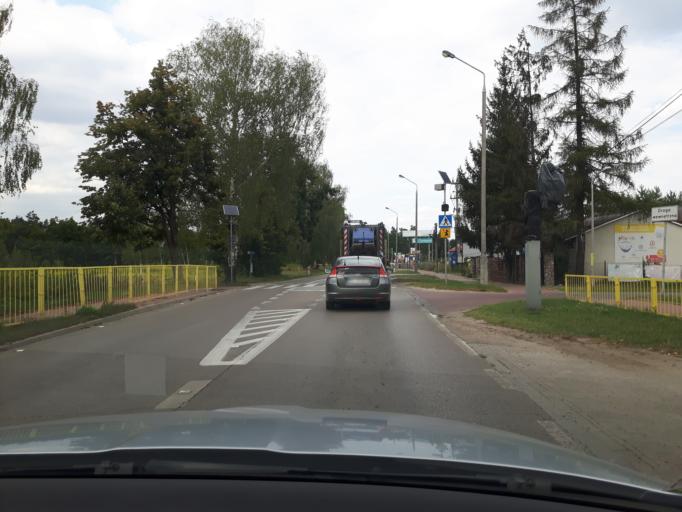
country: PL
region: Masovian Voivodeship
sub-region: Powiat legionowski
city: Stanislawow Pierwszy
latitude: 52.3937
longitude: 21.0337
